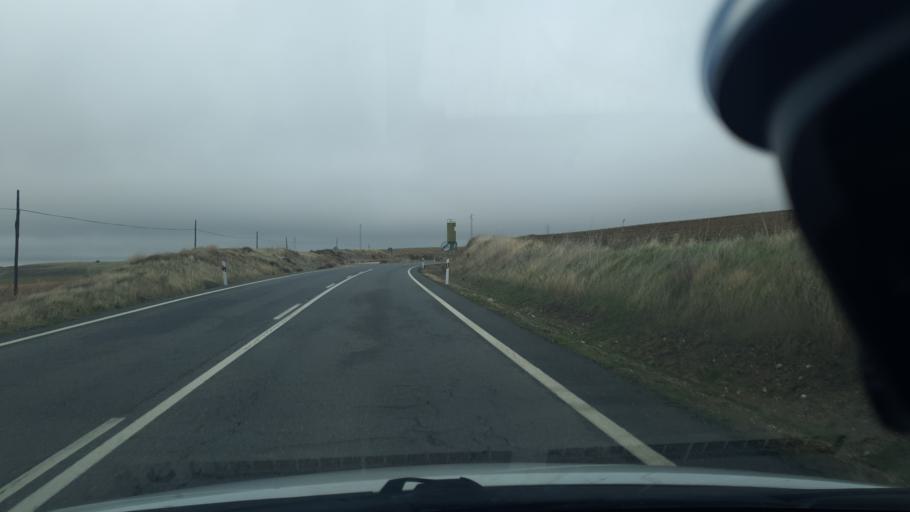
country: ES
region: Castille and Leon
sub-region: Provincia de Segovia
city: Encinillas
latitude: 41.0334
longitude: -4.1400
